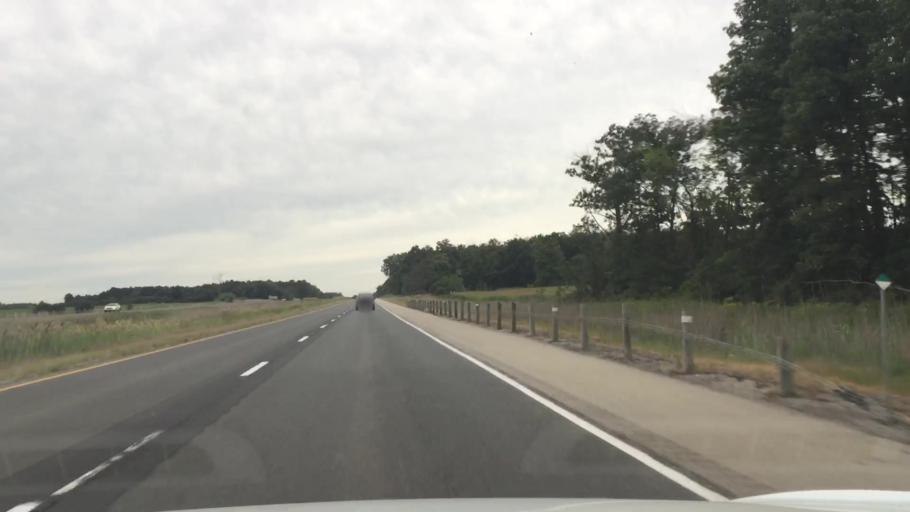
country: CA
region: Ontario
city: Lambton Shores
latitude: 42.9922
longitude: -81.8991
